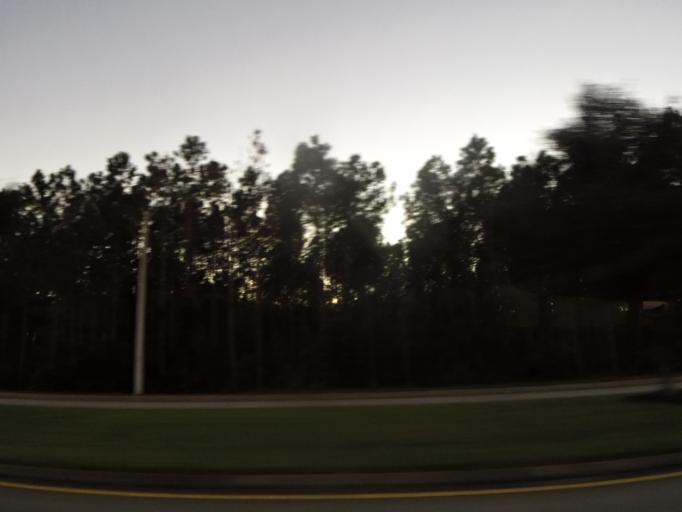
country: US
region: Florida
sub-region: Flagler County
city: Palm Coast
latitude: 29.5934
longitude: -81.2648
